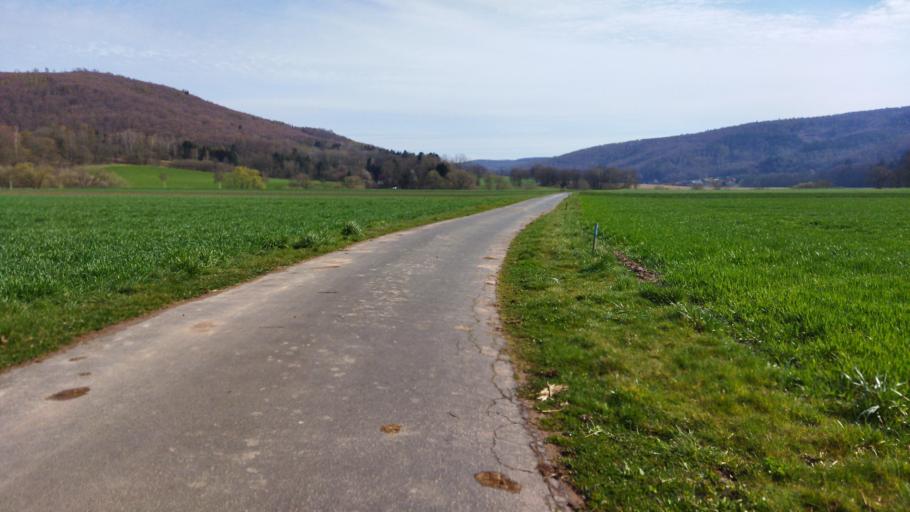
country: DE
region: Lower Saxony
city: Buhren
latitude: 51.5205
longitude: 9.5919
